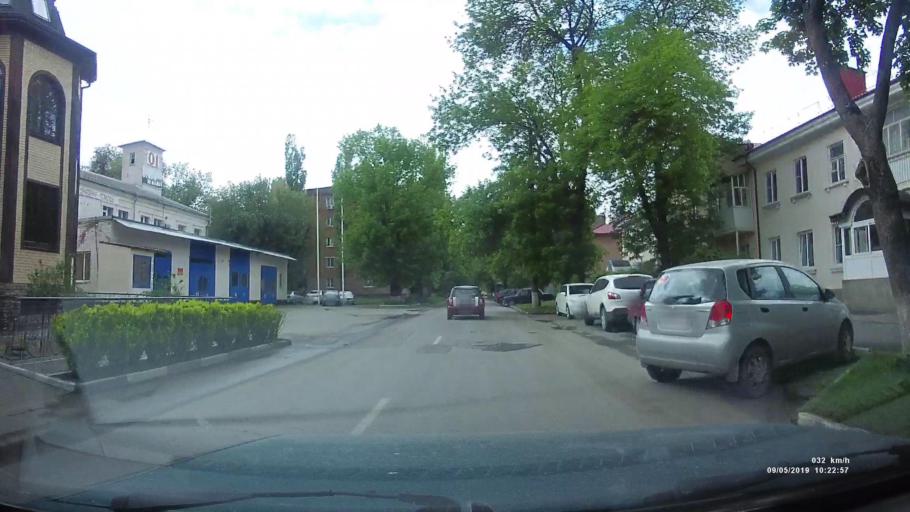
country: RU
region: Rostov
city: Azov
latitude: 47.1036
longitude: 39.4210
